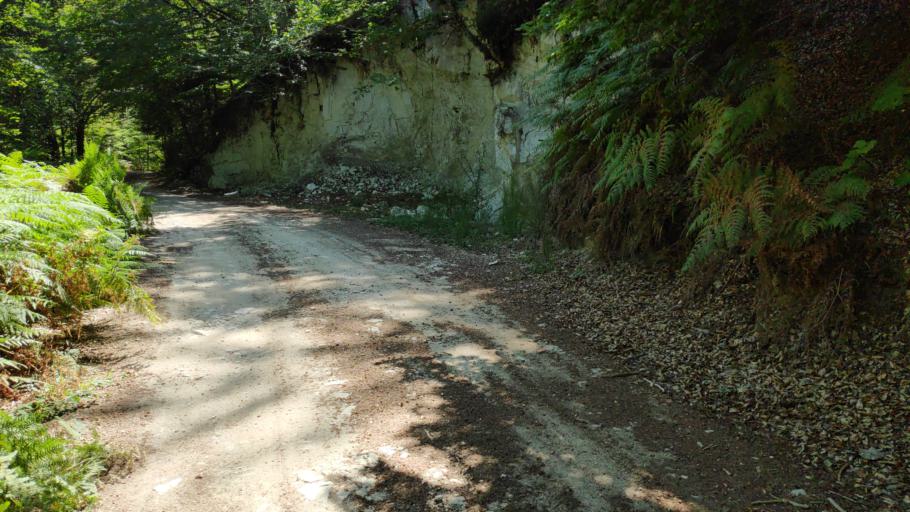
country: IT
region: Calabria
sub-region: Provincia di Vibo-Valentia
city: Mongiana
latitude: 38.5374
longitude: 16.3815
